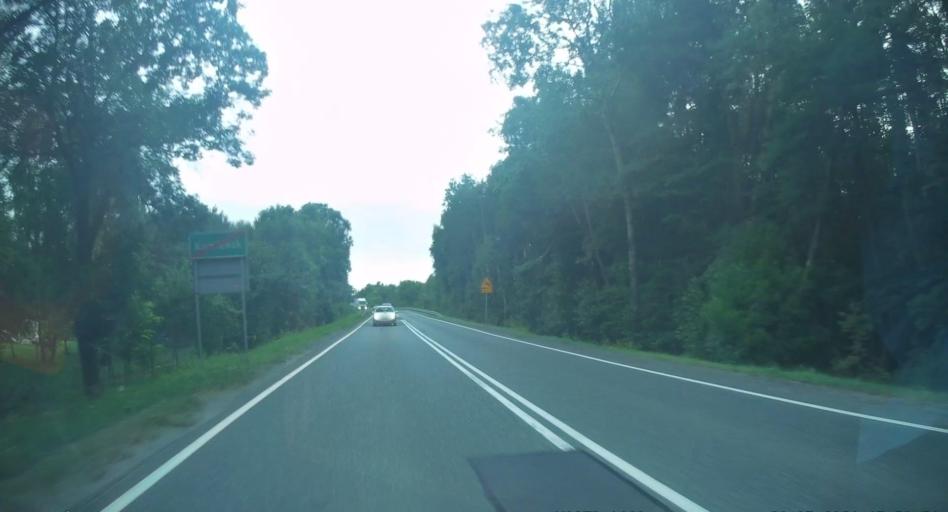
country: PL
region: Lodz Voivodeship
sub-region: Powiat radomszczanski
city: Kamiensk
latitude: 51.1872
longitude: 19.4960
